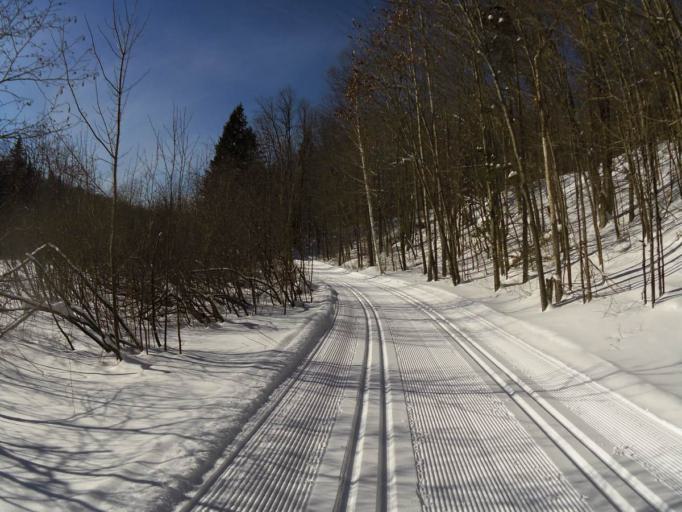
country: CA
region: Quebec
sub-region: Outaouais
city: Wakefield
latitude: 45.6239
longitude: -75.9969
